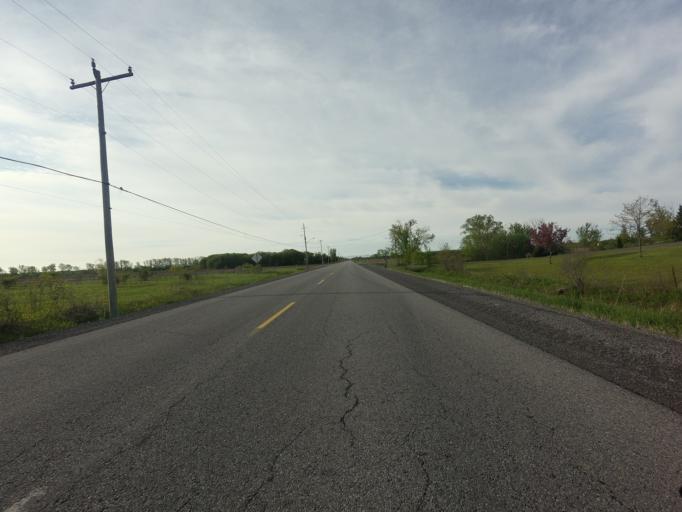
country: CA
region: Ontario
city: Ottawa
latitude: 45.3065
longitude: -75.4571
